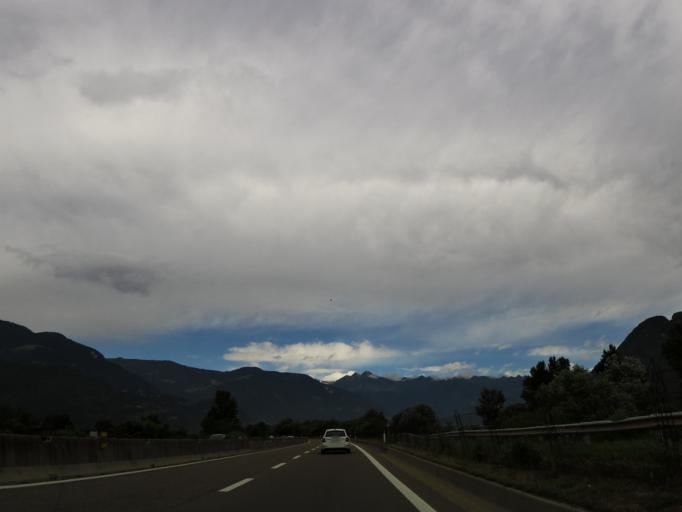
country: IT
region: Trentino-Alto Adige
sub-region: Bolzano
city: Gargazzone
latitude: 46.5658
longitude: 11.2127
